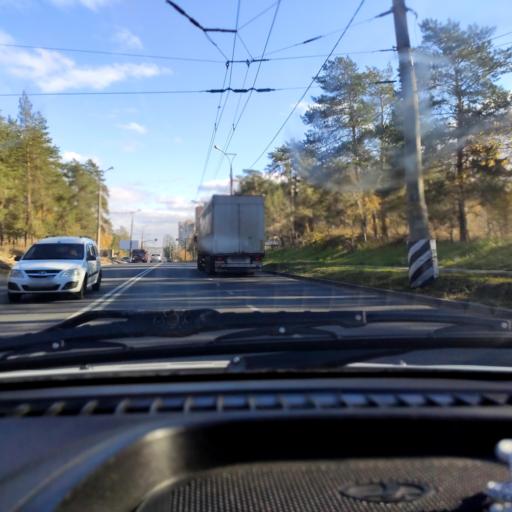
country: RU
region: Samara
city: Zhigulevsk
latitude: 53.4878
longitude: 49.4631
